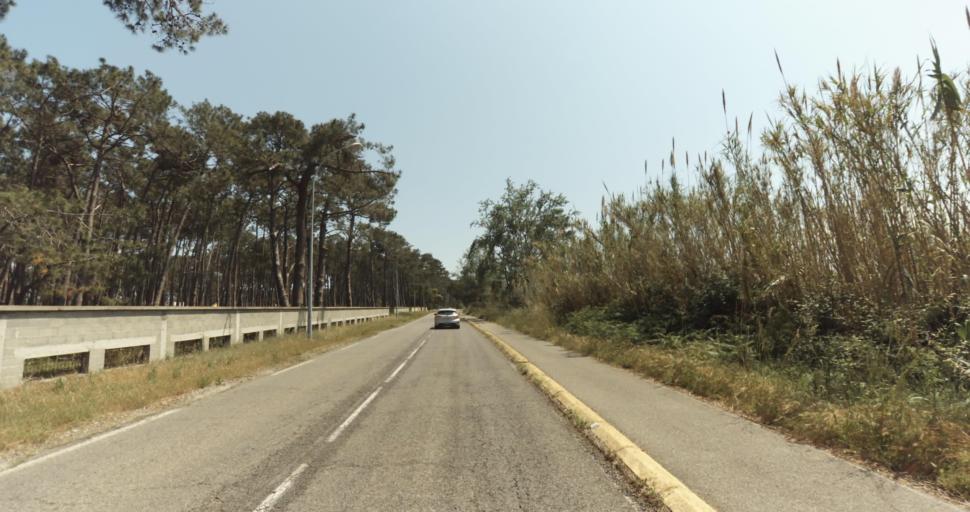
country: FR
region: Corsica
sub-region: Departement de la Haute-Corse
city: Biguglia
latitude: 42.6204
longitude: 9.4746
